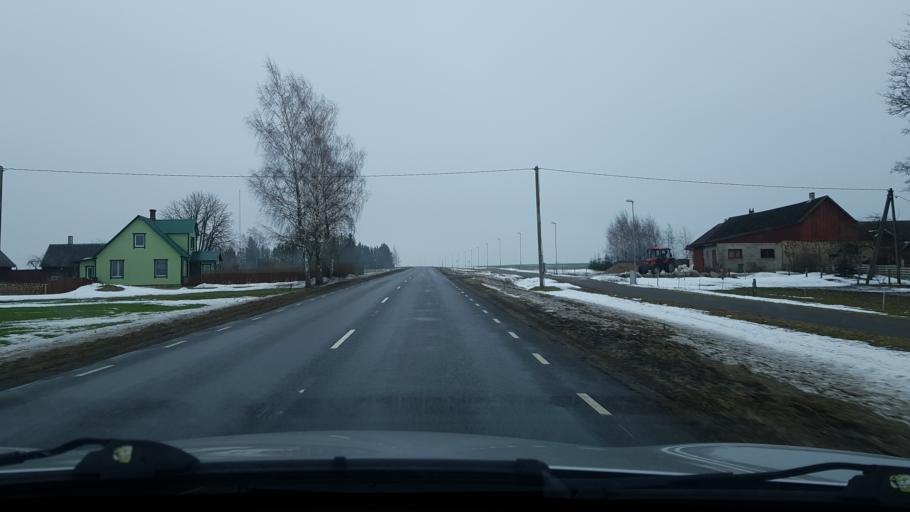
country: EE
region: Valgamaa
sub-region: Torva linn
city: Torva
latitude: 58.2233
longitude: 25.8935
